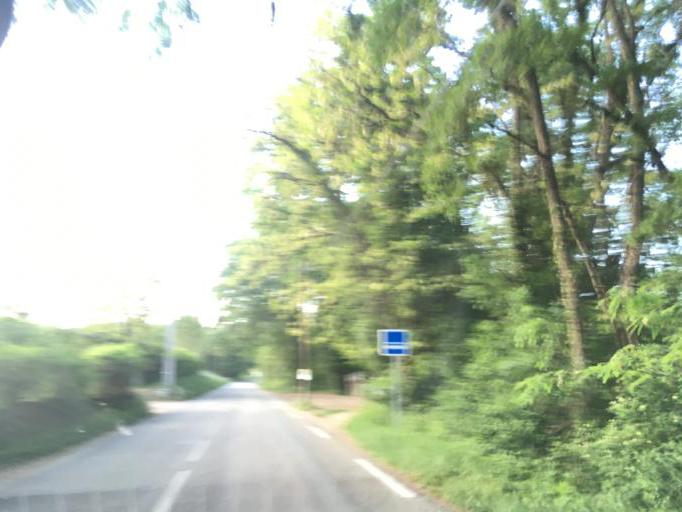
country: FR
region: Provence-Alpes-Cote d'Azur
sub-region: Departement du Var
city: Carces
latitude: 43.5034
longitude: 6.2286
